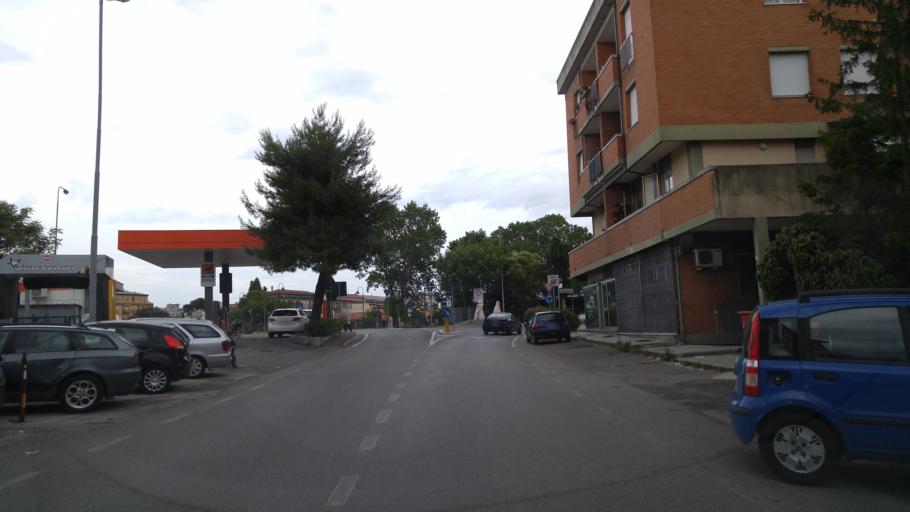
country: IT
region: The Marches
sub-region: Provincia di Pesaro e Urbino
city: Pesaro
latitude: 43.9165
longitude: 12.9021
